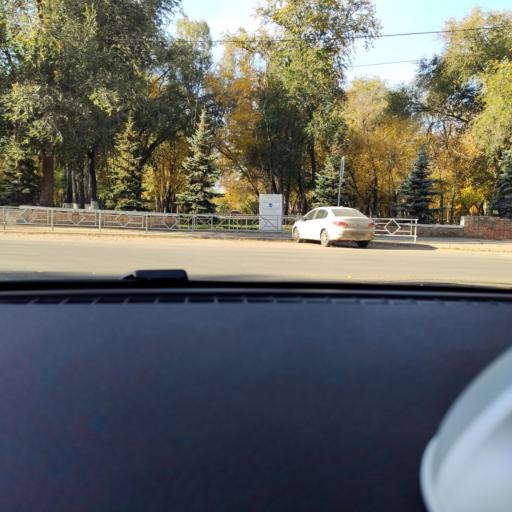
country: RU
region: Samara
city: Samara
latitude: 53.2249
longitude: 50.2453
